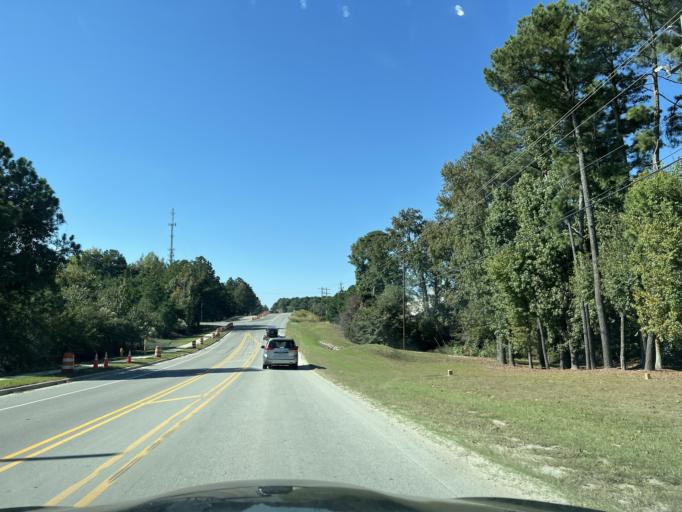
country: US
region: North Carolina
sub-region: Wake County
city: Garner
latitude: 35.7020
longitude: -78.5781
